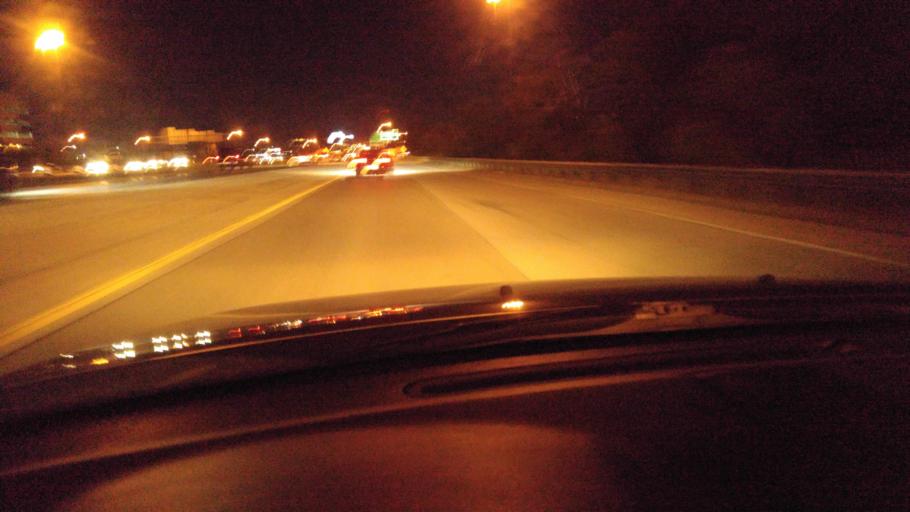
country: US
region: Ohio
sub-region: Franklin County
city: Grandview Heights
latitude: 39.9790
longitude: -83.0214
